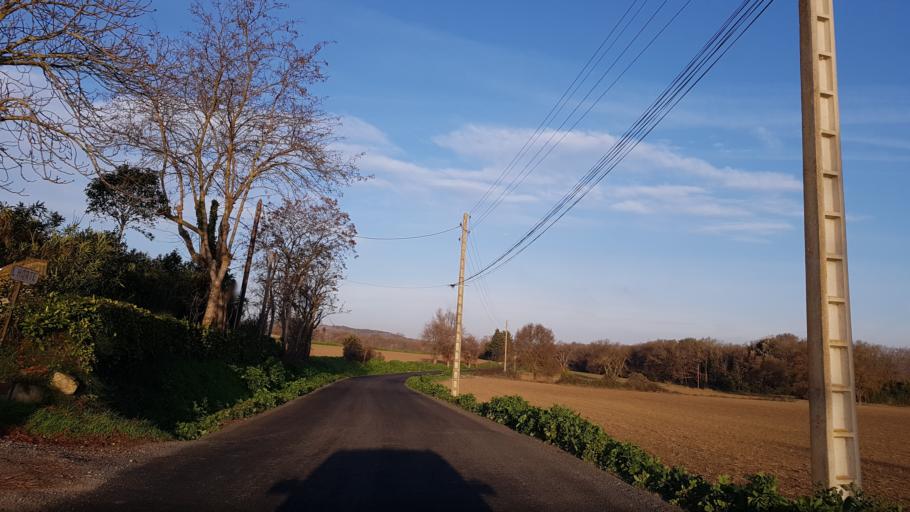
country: FR
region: Languedoc-Roussillon
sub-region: Departement de l'Aude
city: Villeneuve-la-Comptal
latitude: 43.2776
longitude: 1.9423
